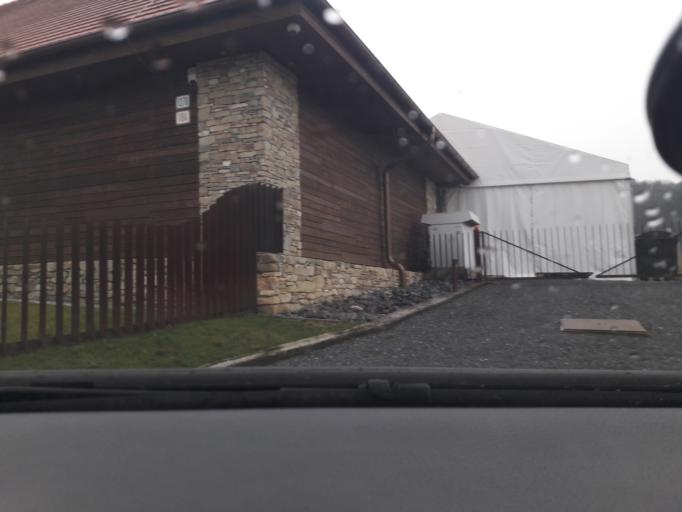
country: SK
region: Trnavsky
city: Smolenice
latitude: 48.5104
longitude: 17.4375
